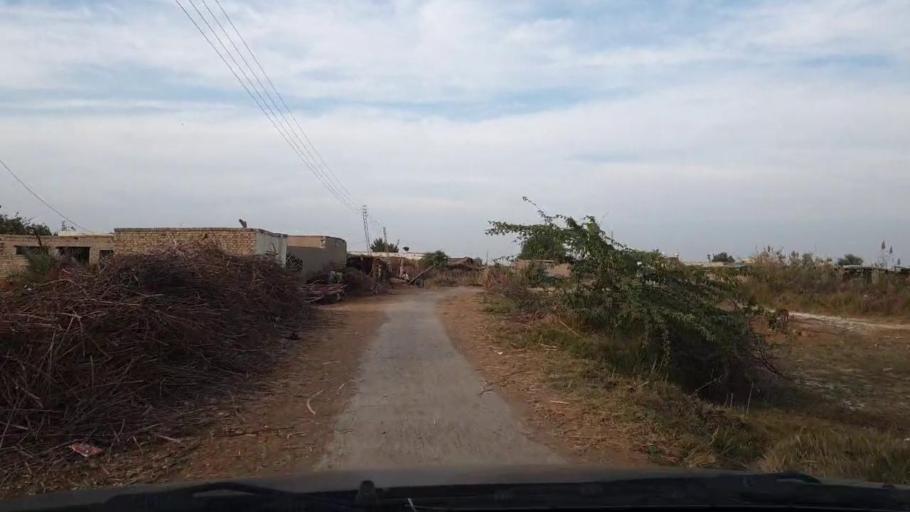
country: PK
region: Sindh
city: Khadro
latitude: 26.1673
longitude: 68.7262
